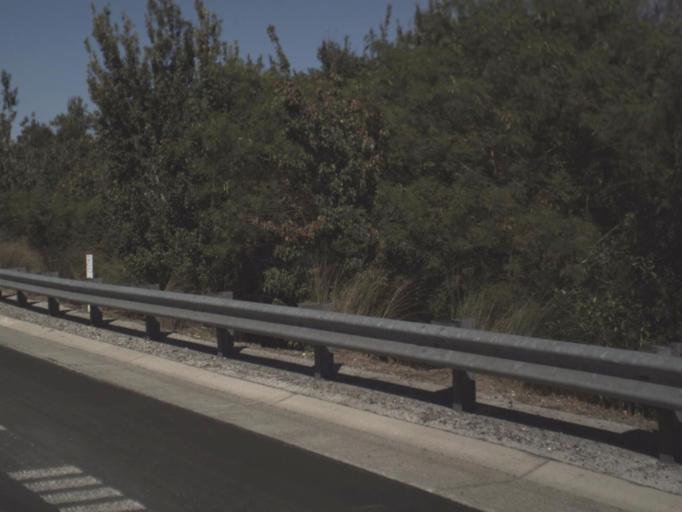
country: US
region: Florida
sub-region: Seminole County
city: Lake Mary
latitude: 28.7816
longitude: -81.3000
